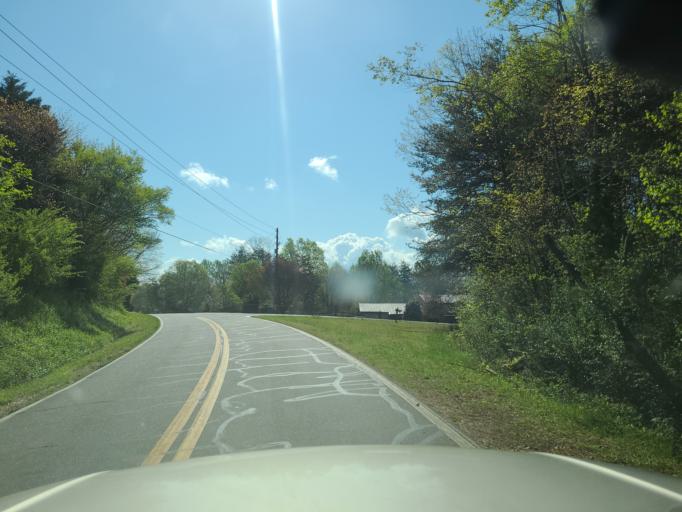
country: US
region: North Carolina
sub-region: Rutherford County
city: Spindale
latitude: 35.2966
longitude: -81.9621
